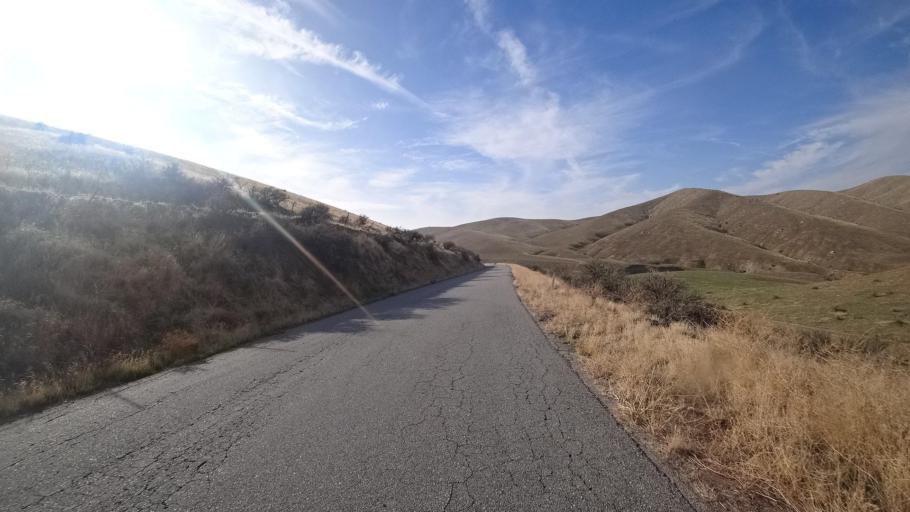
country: US
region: California
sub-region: Kern County
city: Bear Valley Springs
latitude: 35.2807
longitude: -118.6793
